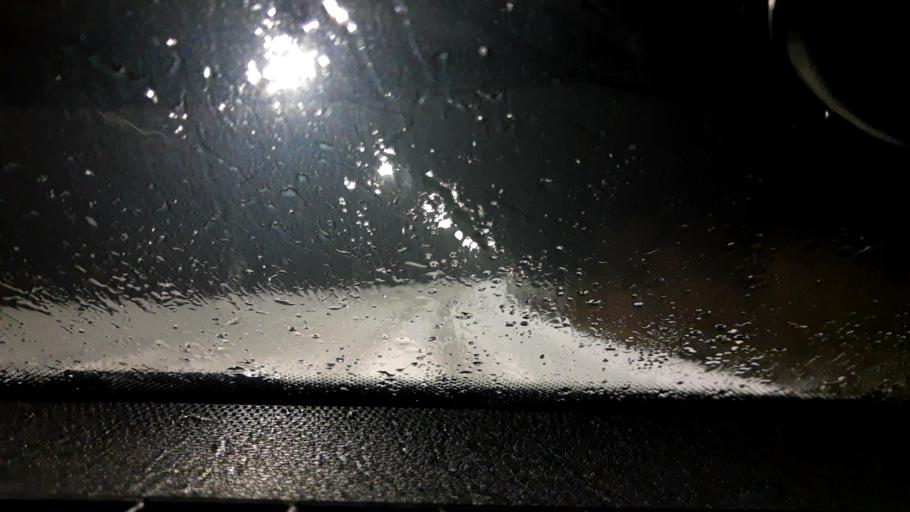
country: RU
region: Bashkortostan
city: Ulukulevo
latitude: 54.5651
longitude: 56.3387
